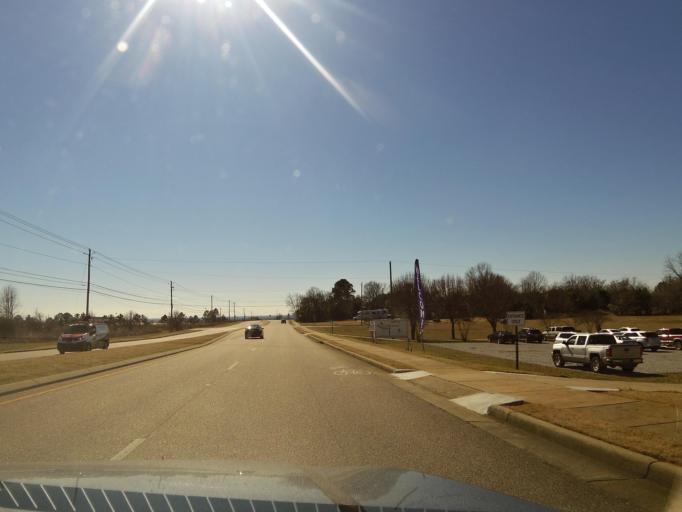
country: US
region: Alabama
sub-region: Elmore County
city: Millbrook
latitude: 32.4664
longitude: -86.4034
